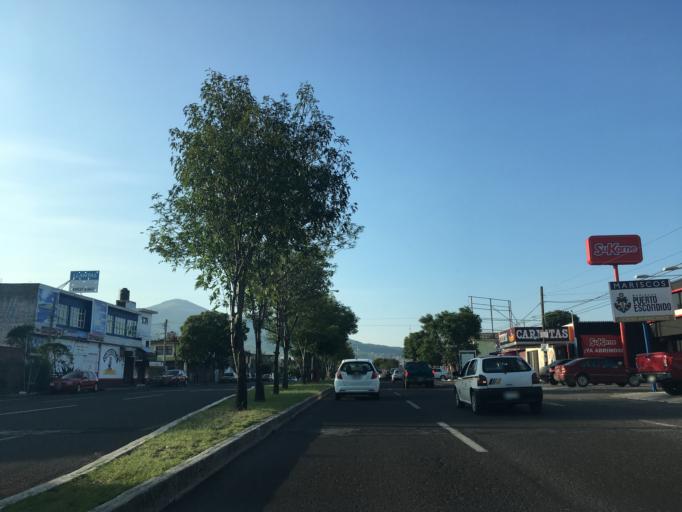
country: MX
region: Michoacan
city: Morelia
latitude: 19.7071
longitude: -101.2256
